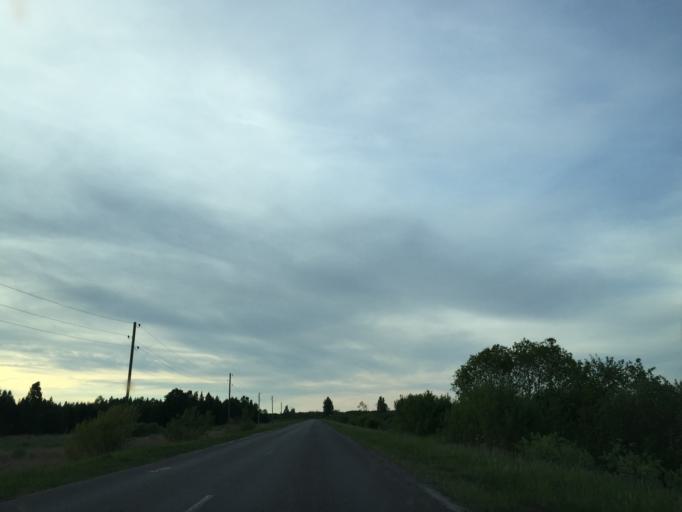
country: LV
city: Tireli
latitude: 56.8217
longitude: 23.5696
